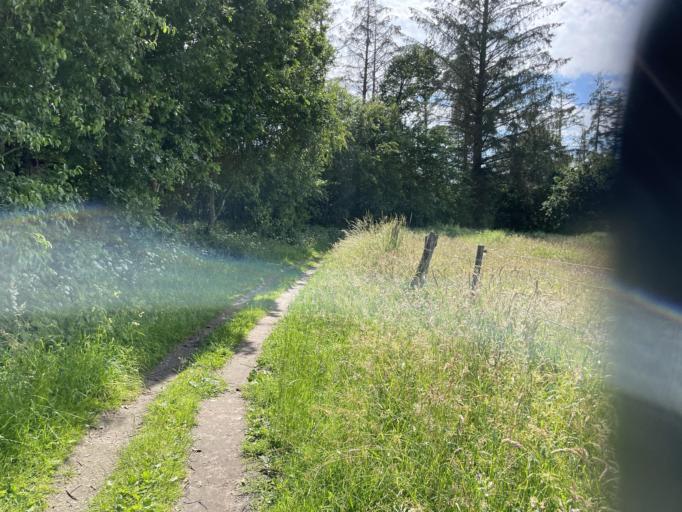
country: DE
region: Schleswig-Holstein
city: Mildstedt
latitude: 54.4727
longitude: 9.1076
